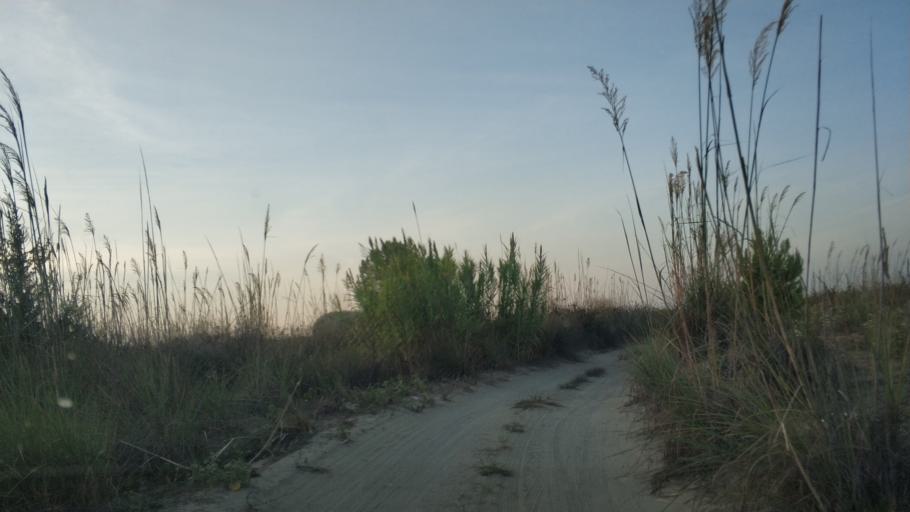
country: AL
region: Fier
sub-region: Rrethi i Lushnjes
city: Divjake
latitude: 40.9548
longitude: 19.4713
